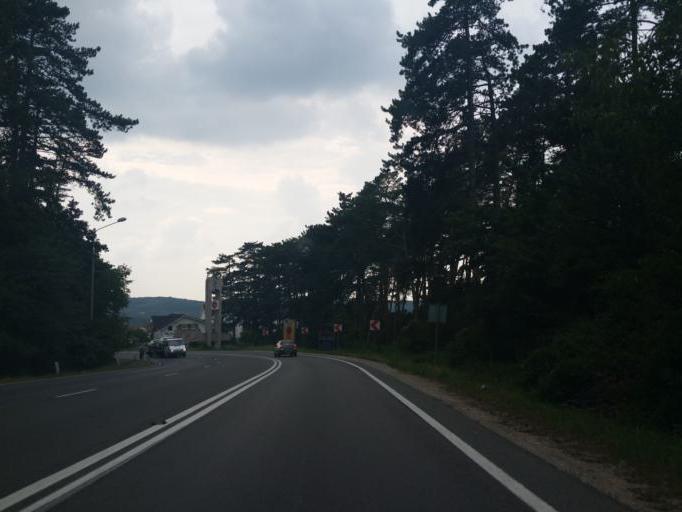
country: RO
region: Salaj
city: Zalau
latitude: 47.1676
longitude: 23.0774
